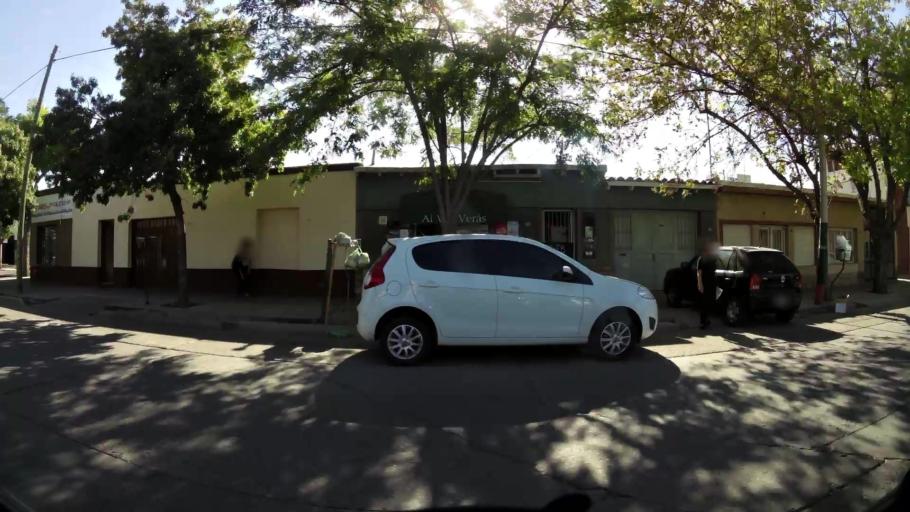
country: AR
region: Mendoza
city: Mendoza
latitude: -32.9094
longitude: -68.8324
